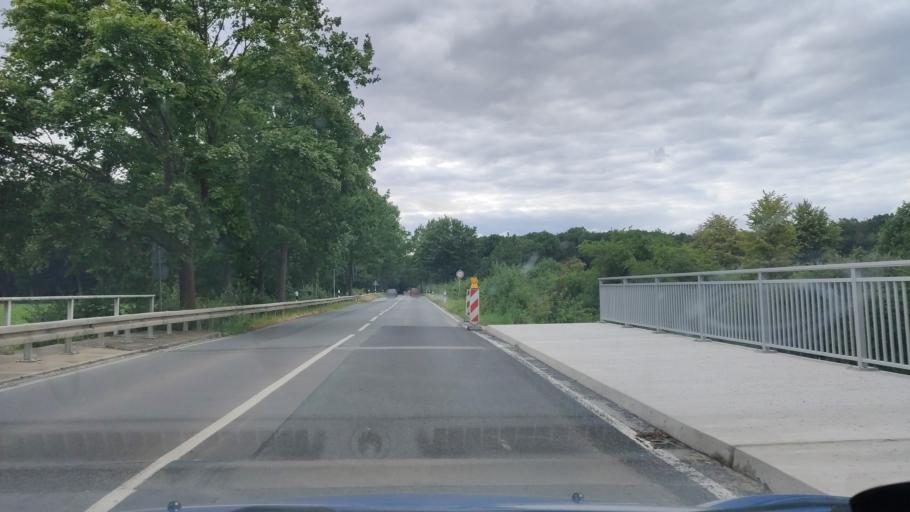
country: DE
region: Lower Saxony
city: Ronnenberg
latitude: 52.3103
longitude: 9.6786
